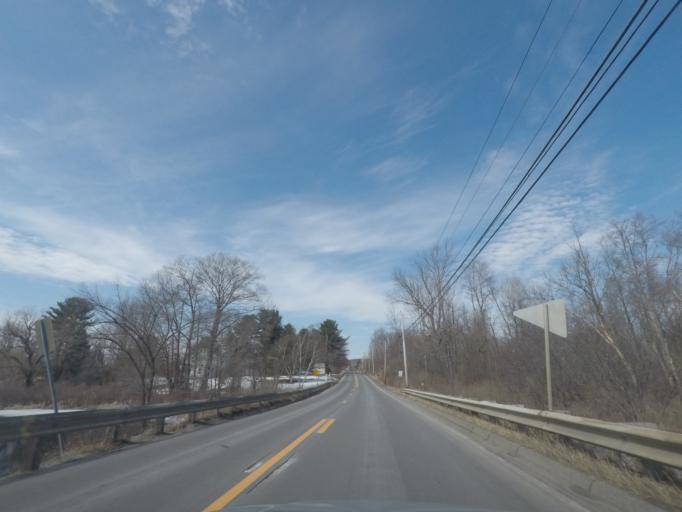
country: US
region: Massachusetts
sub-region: Berkshire County
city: West Stockbridge
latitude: 42.3420
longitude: -73.3755
